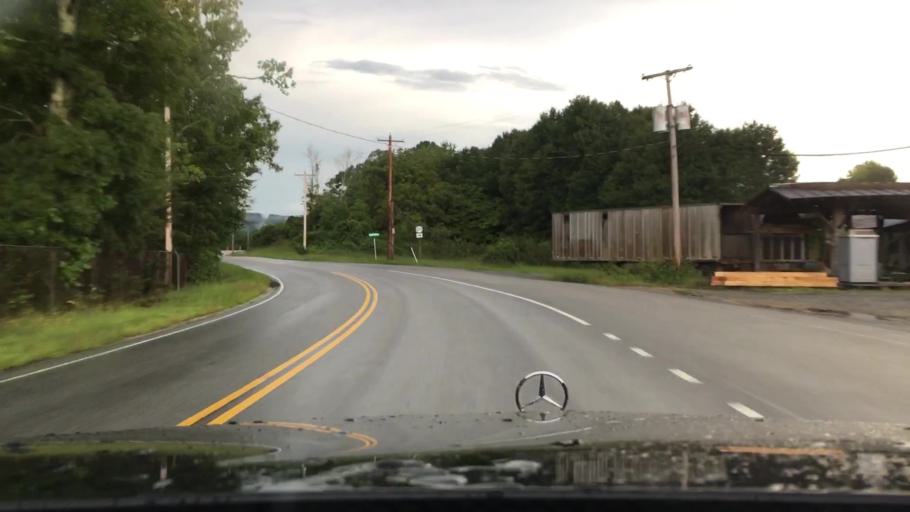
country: US
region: Virginia
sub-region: Amherst County
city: Amherst
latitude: 37.7137
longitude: -79.0228
